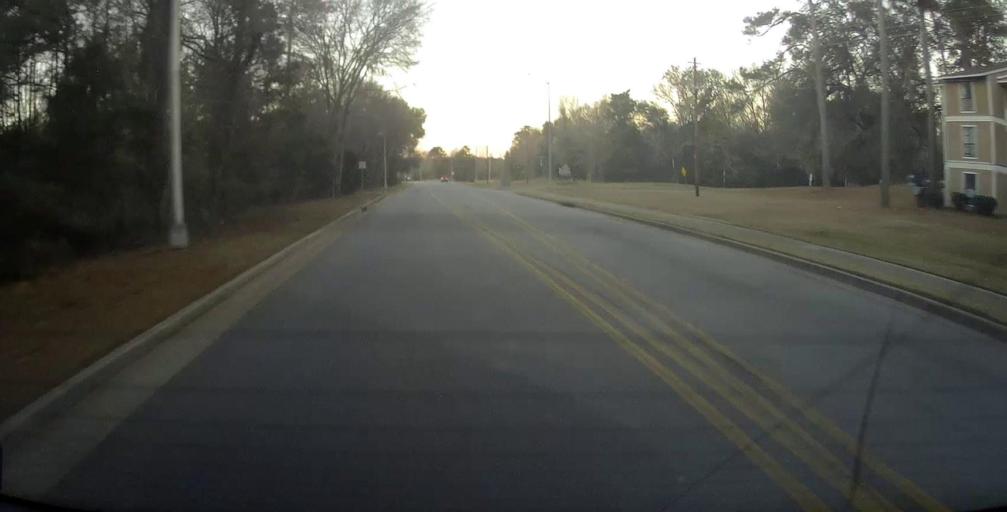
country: US
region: Georgia
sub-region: Dougherty County
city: Albany
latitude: 31.5370
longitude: -84.1366
